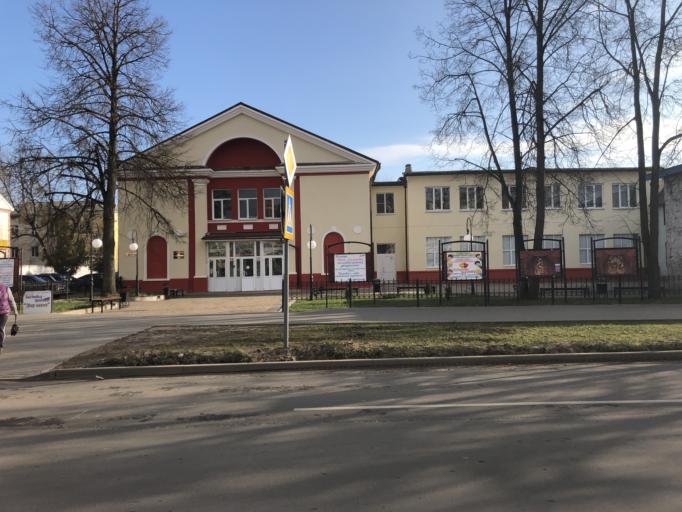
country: RU
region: Tverskaya
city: Rzhev
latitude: 56.2565
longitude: 34.3282
